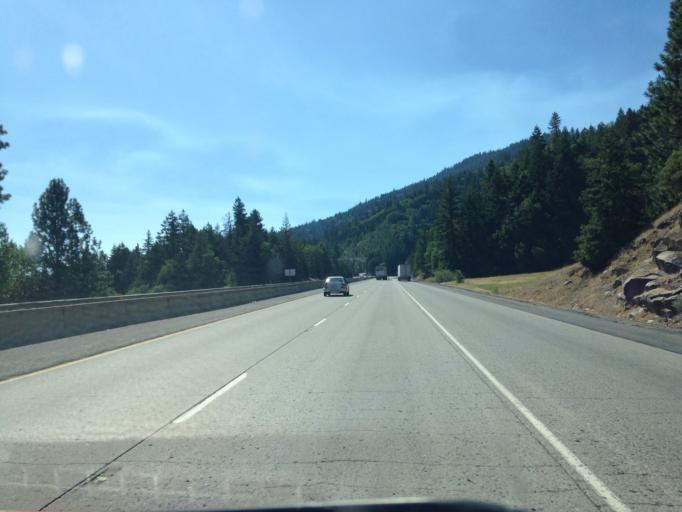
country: US
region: Oregon
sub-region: Jackson County
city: Ashland
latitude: 42.1200
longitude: -122.6243
